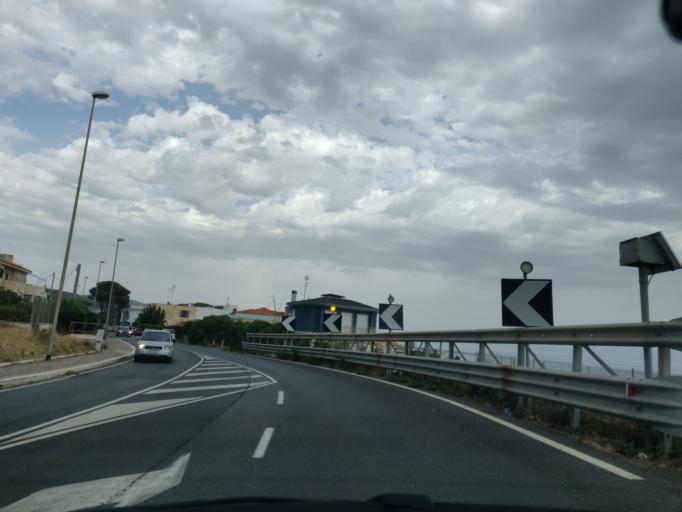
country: IT
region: Latium
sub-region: Citta metropolitana di Roma Capitale
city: Santa Marinella
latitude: 42.0395
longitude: 11.8867
